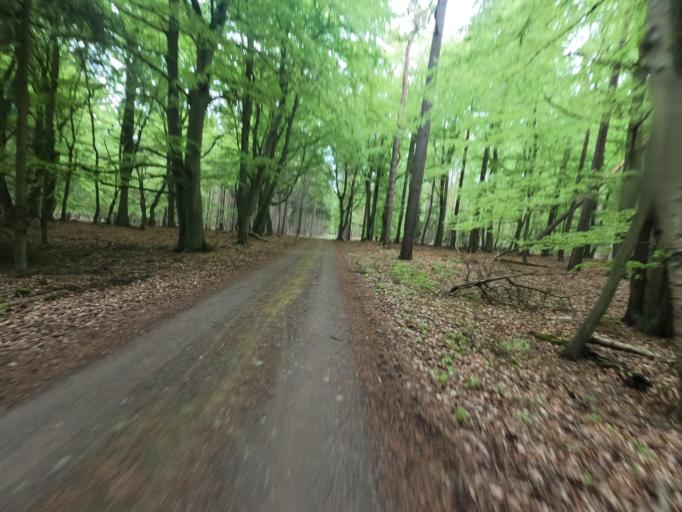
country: DE
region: Mecklenburg-Vorpommern
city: Born
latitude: 54.4138
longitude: 12.4964
